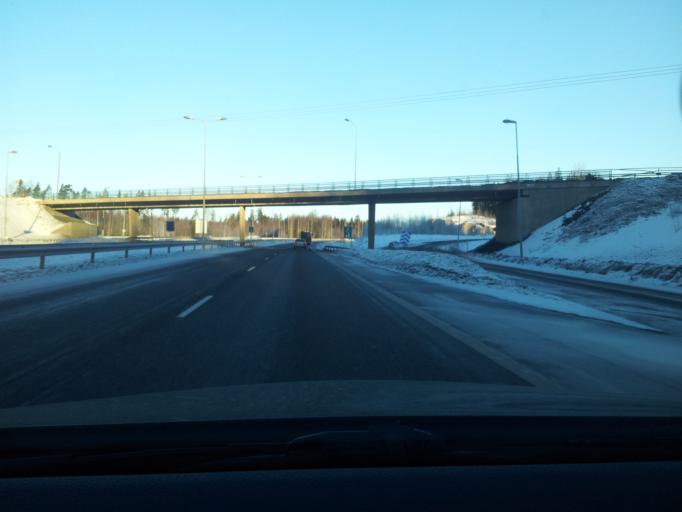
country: FI
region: Uusimaa
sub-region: Helsinki
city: Vihti
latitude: 60.3014
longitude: 24.3564
